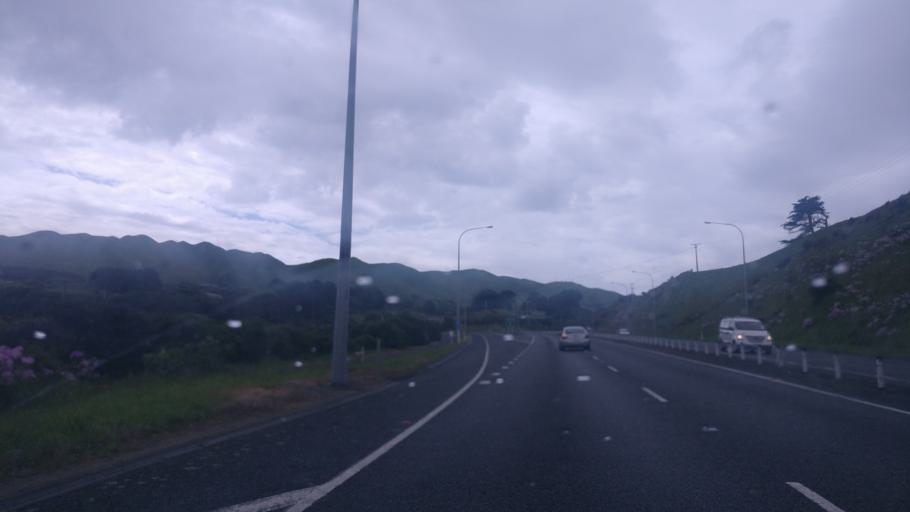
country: NZ
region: Wellington
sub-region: Porirua City
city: Porirua
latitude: -41.0602
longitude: 174.8762
